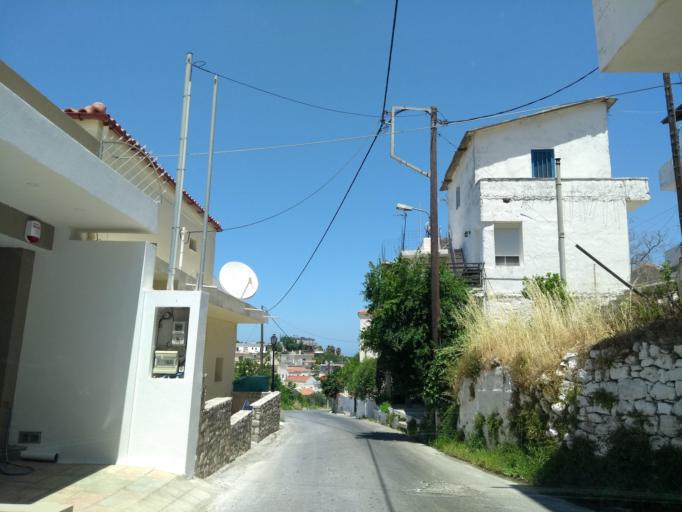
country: GR
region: Crete
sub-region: Nomos Chanias
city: Georgioupolis
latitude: 35.3140
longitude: 24.2982
